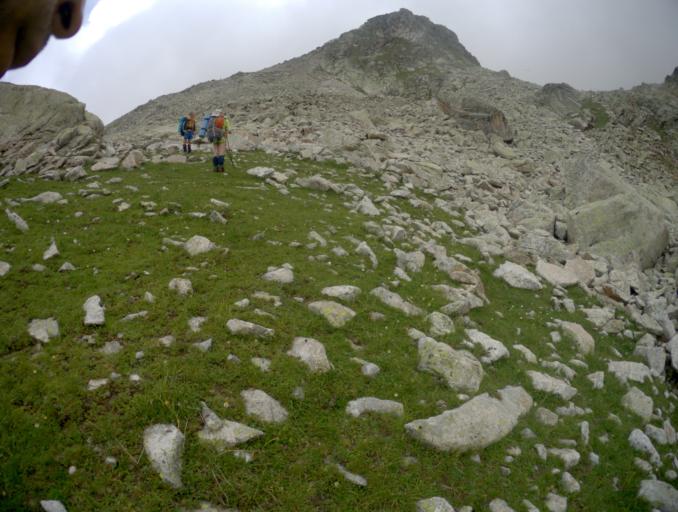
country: RU
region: Karachayevo-Cherkesiya
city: Uchkulan
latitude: 43.2831
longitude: 42.1018
